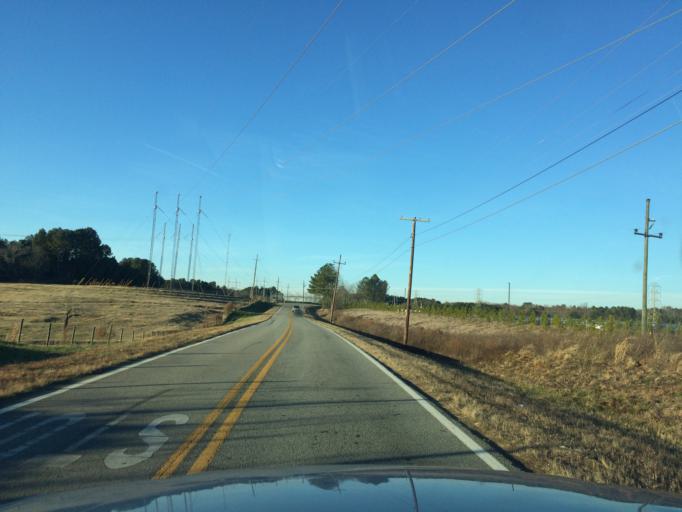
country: US
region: Georgia
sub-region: Barrow County
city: Winder
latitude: 33.9877
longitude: -83.7521
